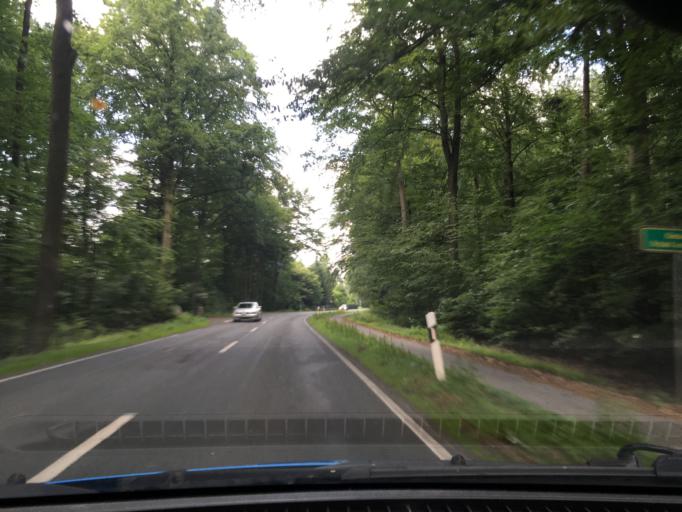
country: DE
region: Lower Saxony
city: Bendestorf
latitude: 53.3479
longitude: 9.9406
